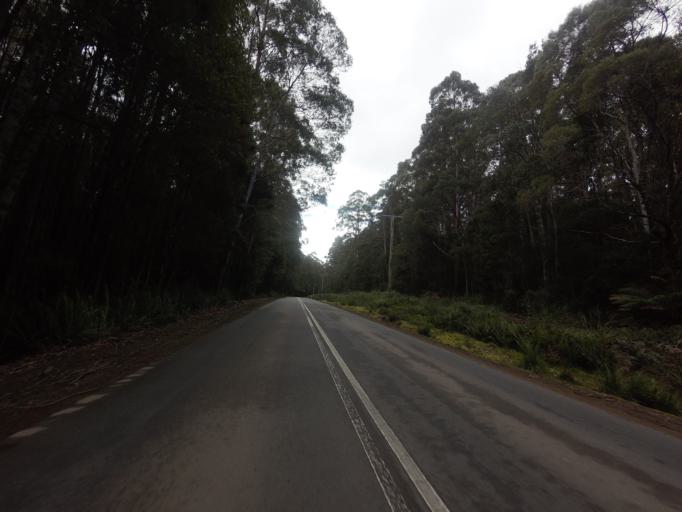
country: AU
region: Tasmania
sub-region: Huon Valley
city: Geeveston
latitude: -43.3872
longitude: 146.9623
